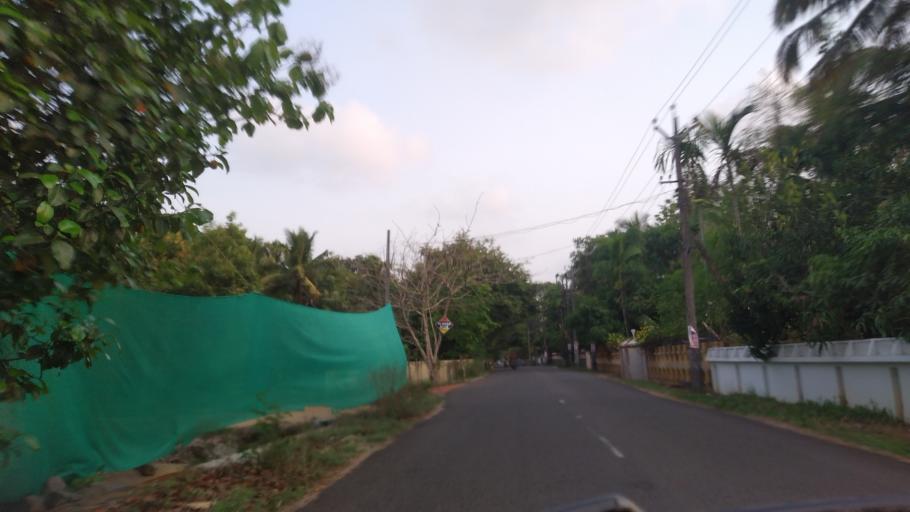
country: IN
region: Kerala
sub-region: Thrissur District
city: Thanniyam
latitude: 10.3394
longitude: 76.1176
